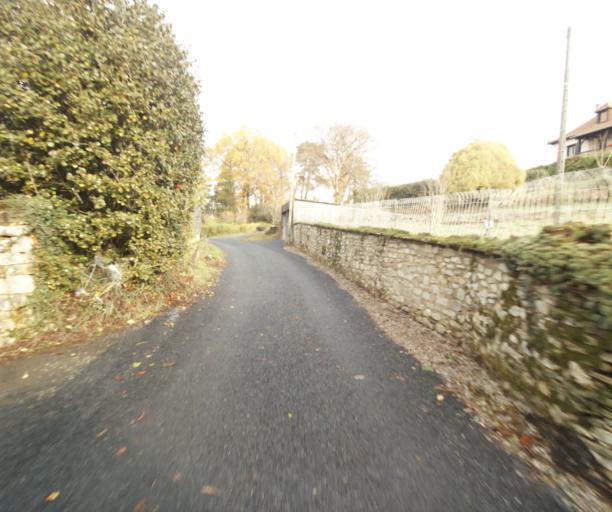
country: FR
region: Limousin
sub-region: Departement de la Correze
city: Cornil
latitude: 45.2035
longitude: 1.7122
